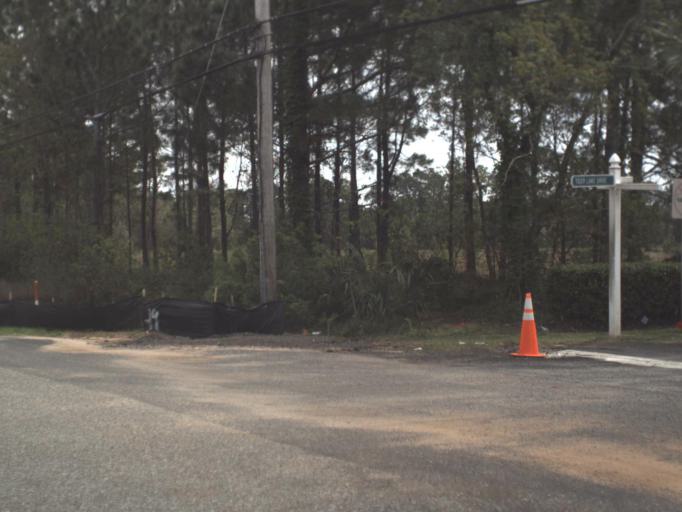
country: US
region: Florida
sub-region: Santa Rosa County
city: Tiger Point
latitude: 30.3911
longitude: -87.0574
